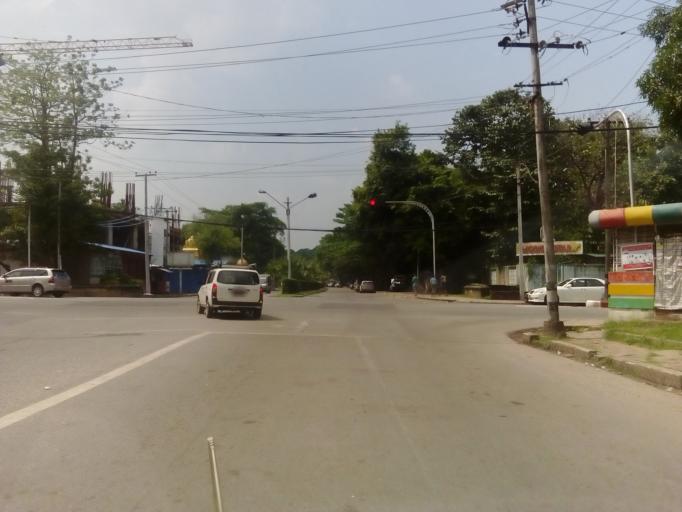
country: MM
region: Yangon
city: Yangon
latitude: 16.7892
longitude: 96.1629
